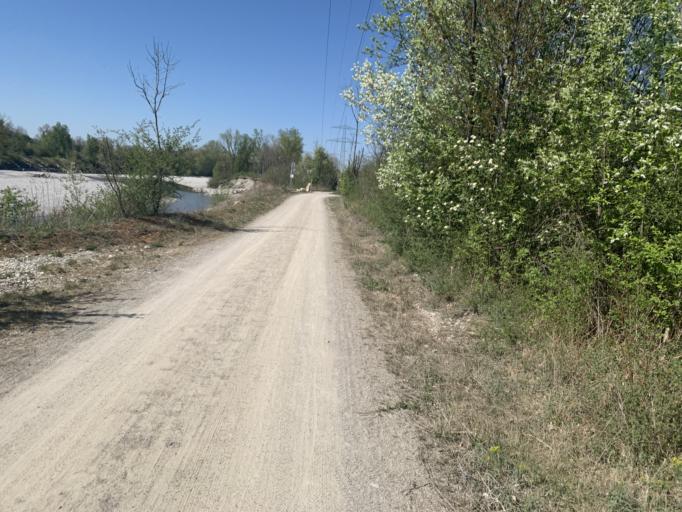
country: DE
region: Bavaria
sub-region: Swabia
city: Gersthofen
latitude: 48.4586
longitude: 10.8854
